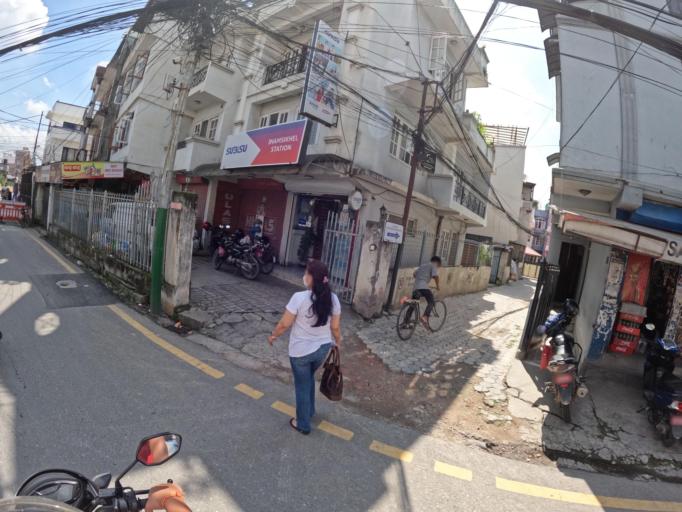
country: NP
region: Central Region
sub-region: Bagmati Zone
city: Patan
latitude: 27.6805
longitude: 85.3102
